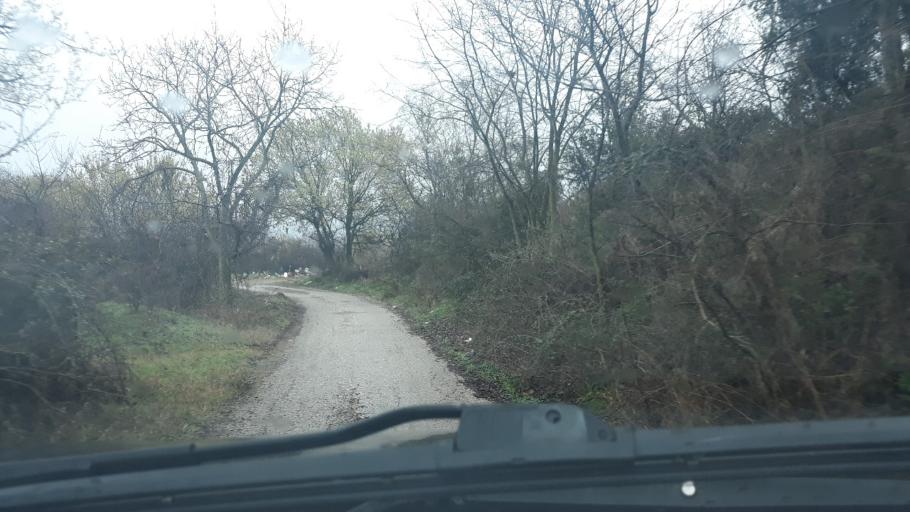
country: MK
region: Valandovo
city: Valandovo
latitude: 41.3182
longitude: 22.5457
